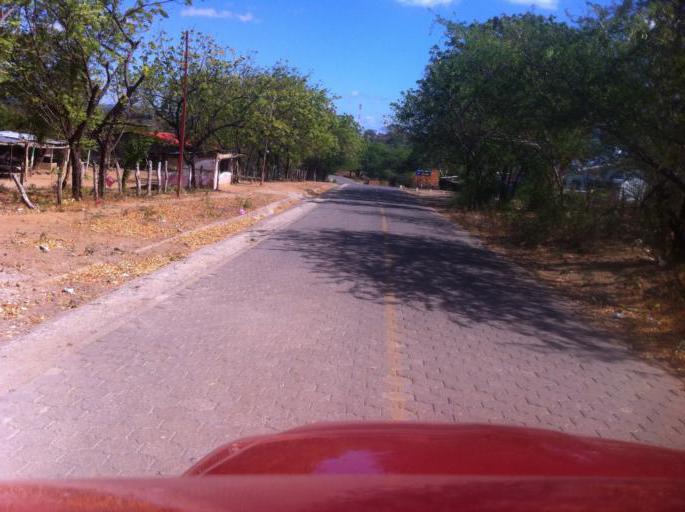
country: NI
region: Carazo
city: El Rosario
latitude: 11.6207
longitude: -86.3288
